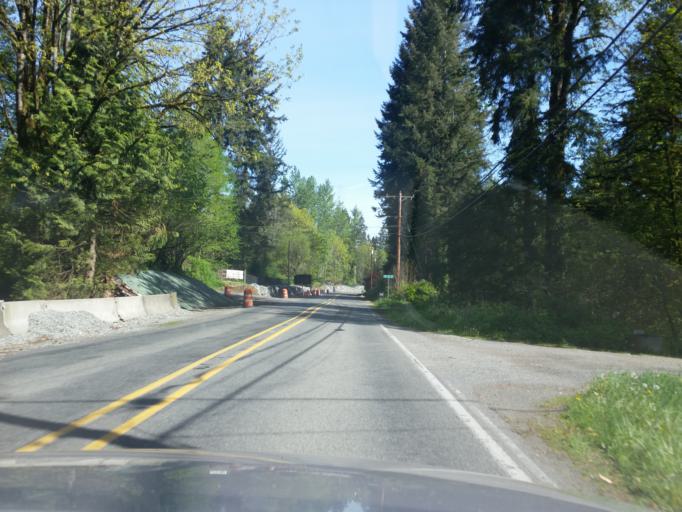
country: US
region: Washington
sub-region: Snohomish County
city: Cathcart
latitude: 47.8404
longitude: -122.1036
